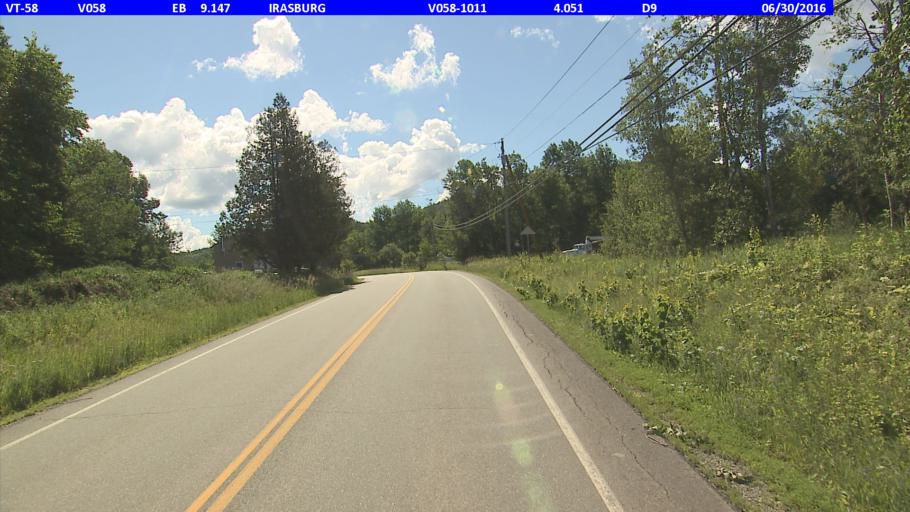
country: US
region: Vermont
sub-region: Orleans County
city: Newport
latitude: 44.8047
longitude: -72.2641
